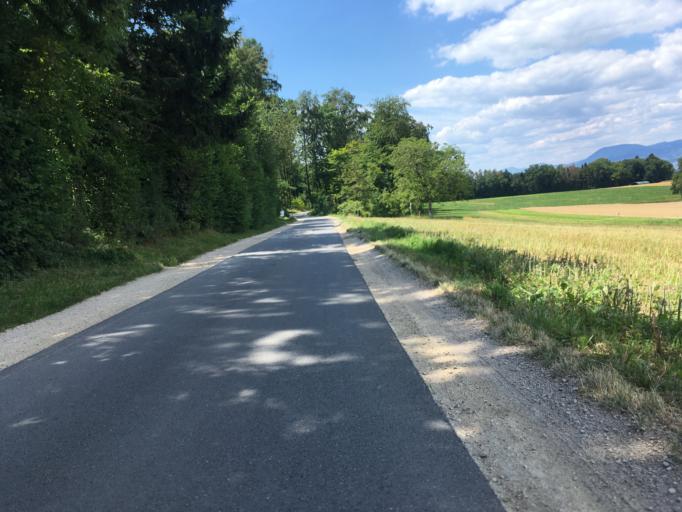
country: CH
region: Fribourg
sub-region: Broye District
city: Domdidier
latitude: 46.9225
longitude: 6.9745
